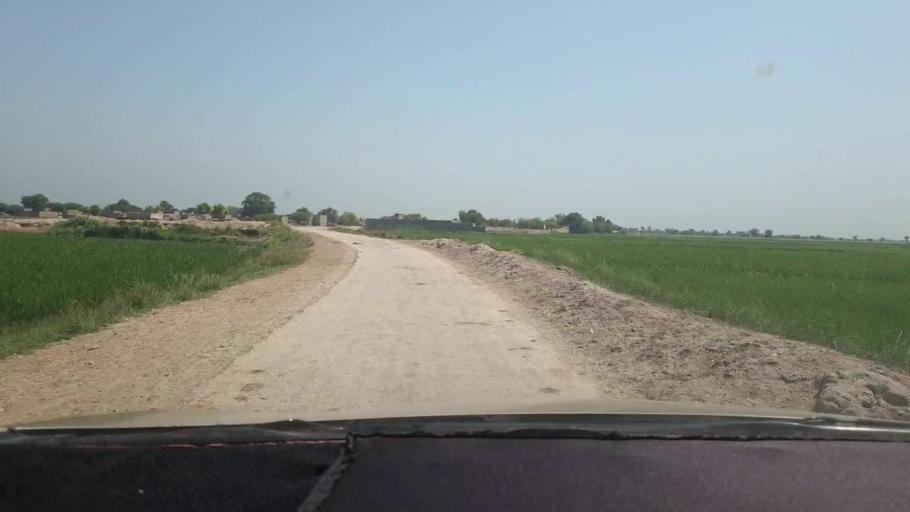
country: PK
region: Sindh
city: Miro Khan
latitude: 27.6730
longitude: 68.0956
